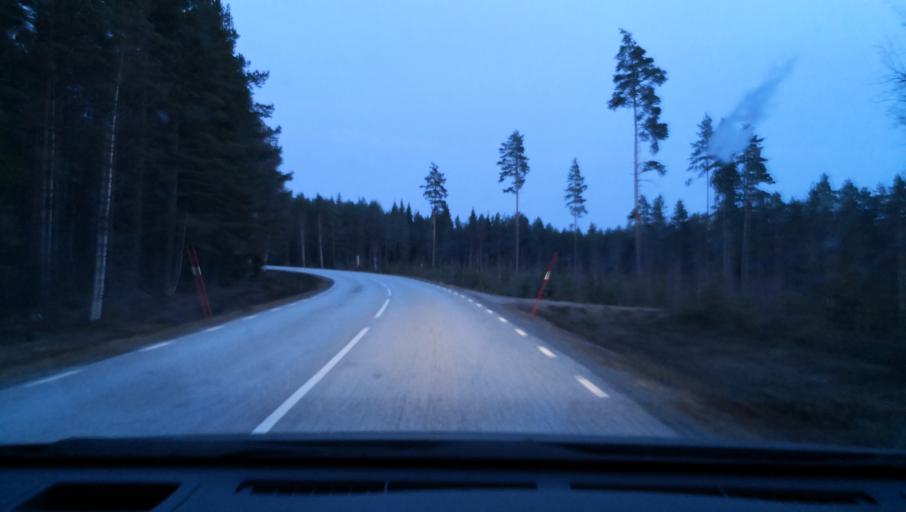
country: SE
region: OErebro
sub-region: Lindesbergs Kommun
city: Frovi
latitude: 59.5925
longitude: 15.3918
